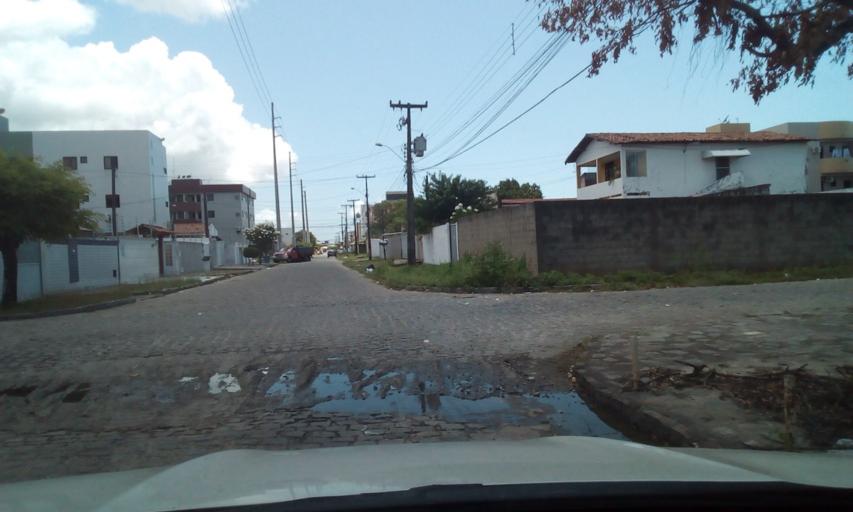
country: BR
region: Paraiba
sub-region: Joao Pessoa
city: Joao Pessoa
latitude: -7.0661
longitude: -34.8469
